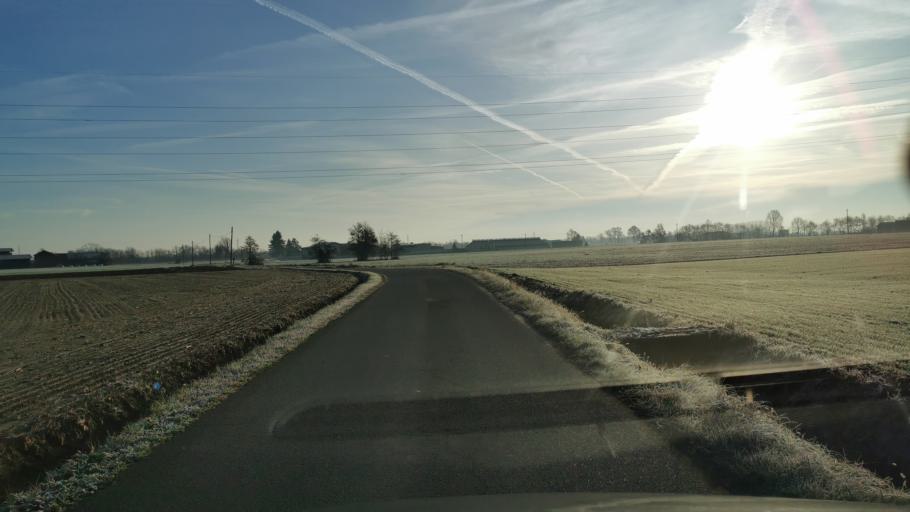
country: IT
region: Piedmont
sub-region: Provincia di Torino
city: Feletto
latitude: 45.2868
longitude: 7.7552
